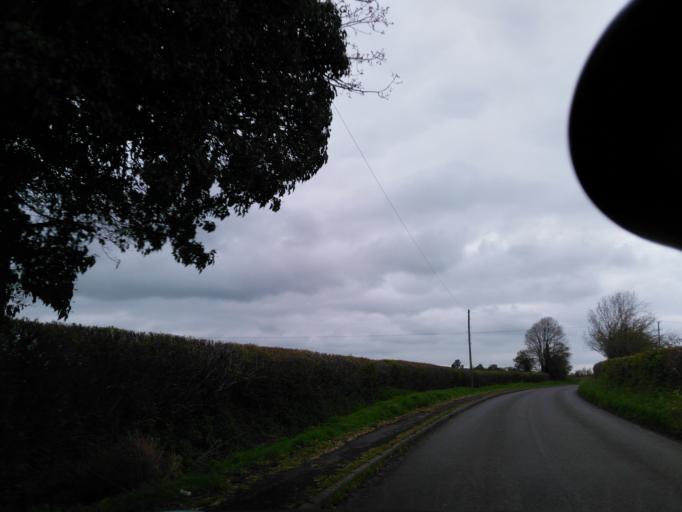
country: GB
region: England
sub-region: Wiltshire
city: Chippenham
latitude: 51.4893
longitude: -2.1333
